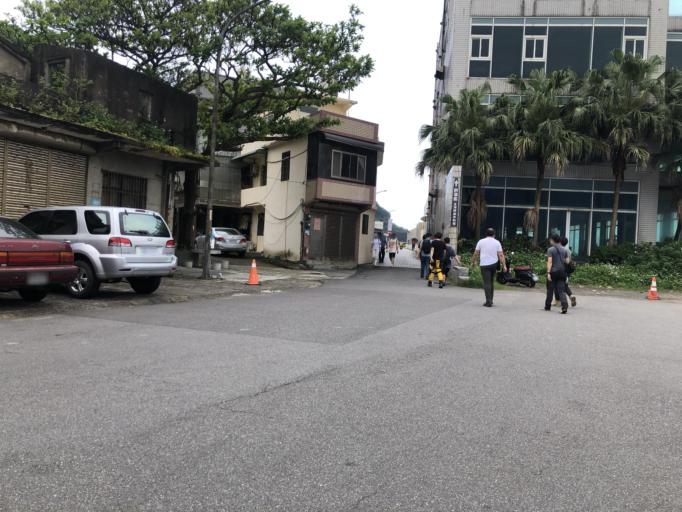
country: TW
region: Taiwan
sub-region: Keelung
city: Keelung
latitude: 25.2239
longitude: 121.6489
